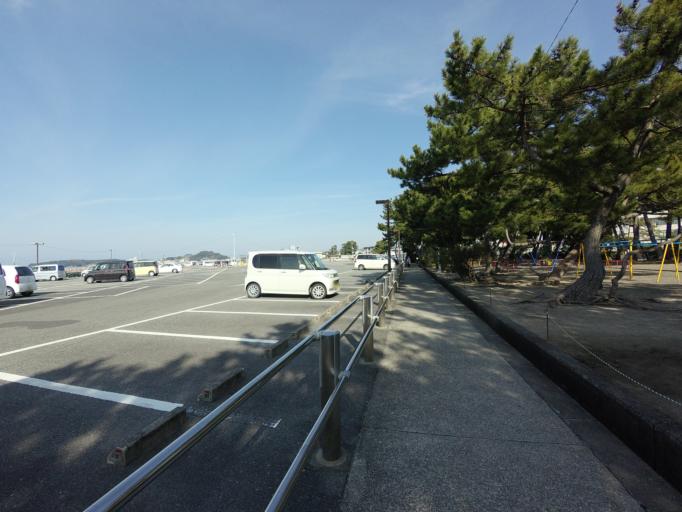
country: JP
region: Wakayama
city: Tanabe
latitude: 33.7267
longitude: 135.3774
